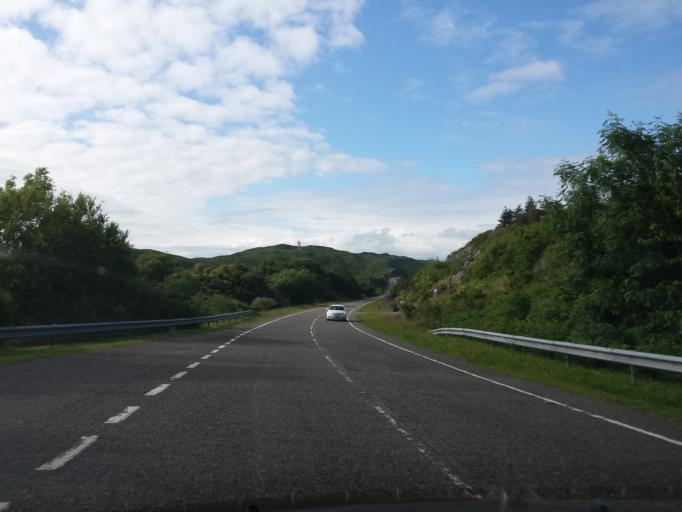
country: GB
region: Scotland
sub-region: Argyll and Bute
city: Isle Of Mull
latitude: 56.9676
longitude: -5.8241
